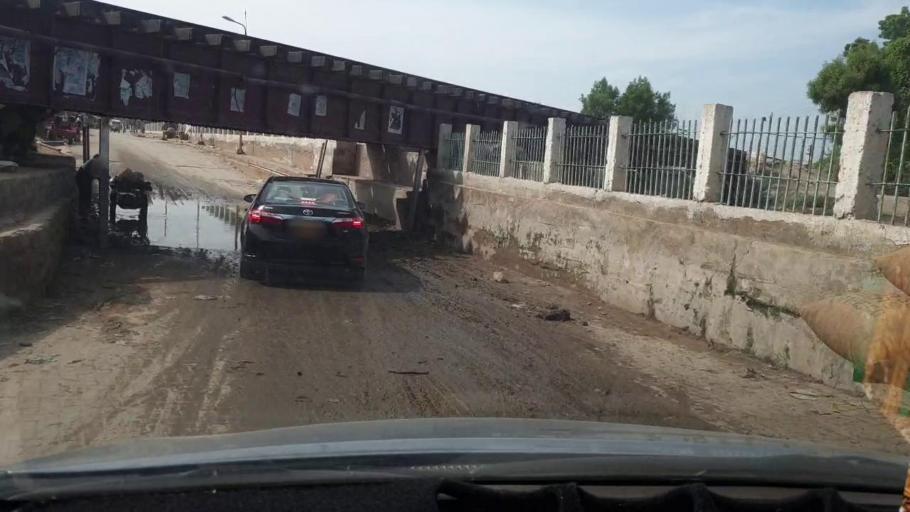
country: PK
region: Sindh
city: Khairpur
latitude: 27.5383
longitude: 68.7516
